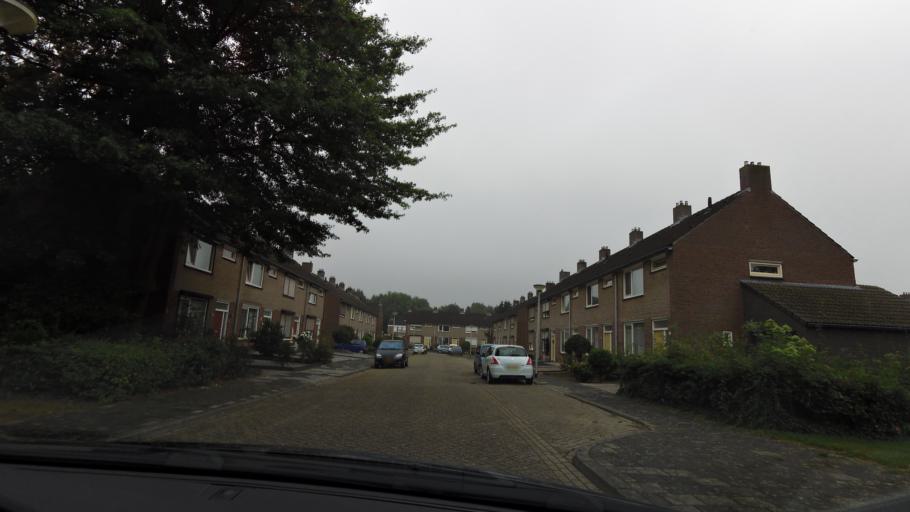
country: NL
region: Limburg
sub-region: Gemeente Heerlen
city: Mariarade
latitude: 50.9236
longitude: 5.9419
